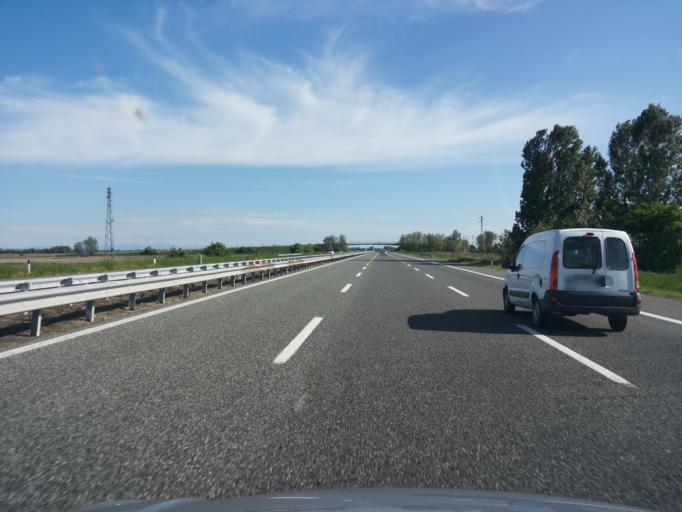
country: IT
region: Piedmont
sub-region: Provincia di Novara
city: Casalbeltrame
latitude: 45.4332
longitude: 8.4617
